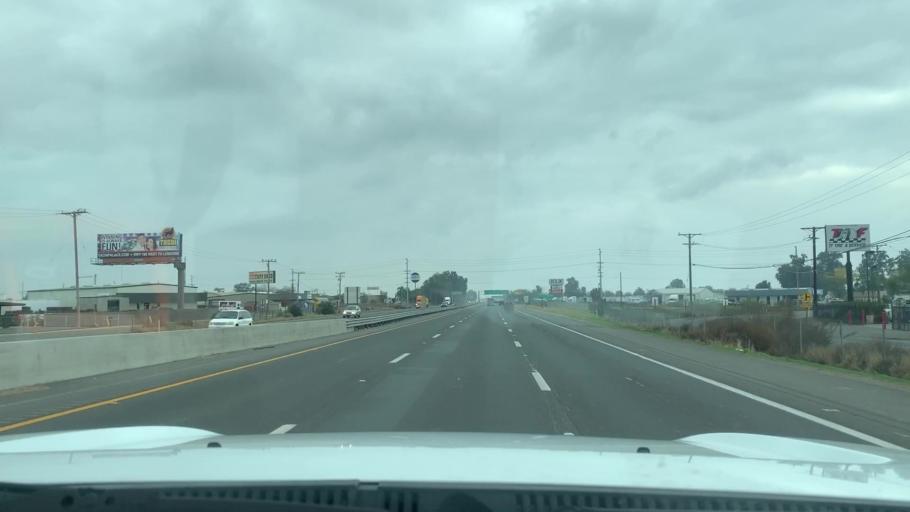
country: US
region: California
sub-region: Tulare County
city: Goshen
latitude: 36.3437
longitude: -119.4217
